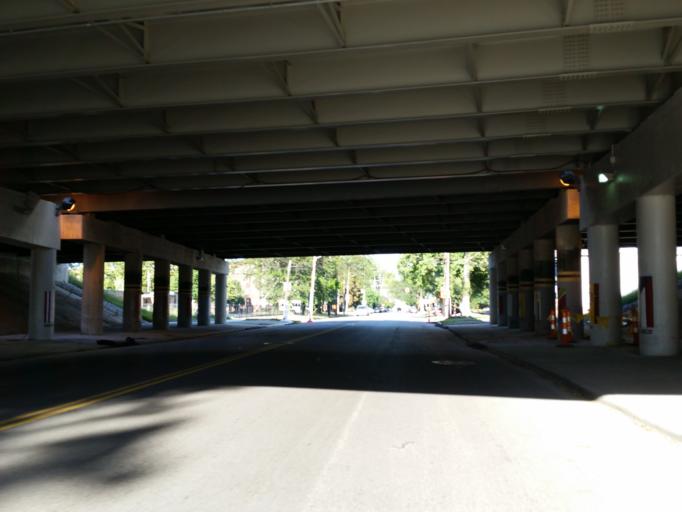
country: US
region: Ohio
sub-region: Cuyahoga County
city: Cleveland
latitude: 41.4796
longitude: -81.6934
